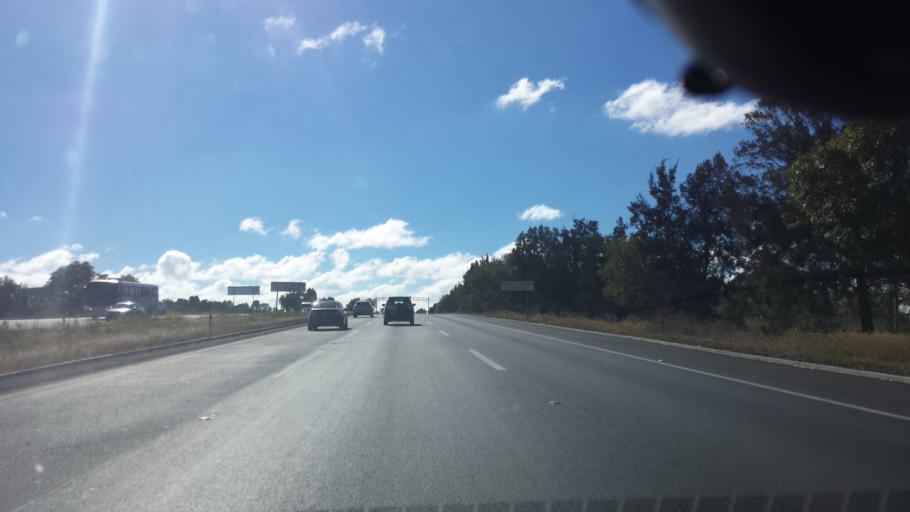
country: MX
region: Mexico
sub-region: Aculco
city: La Presita Segundo Cuartel
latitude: 20.2041
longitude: -99.7853
